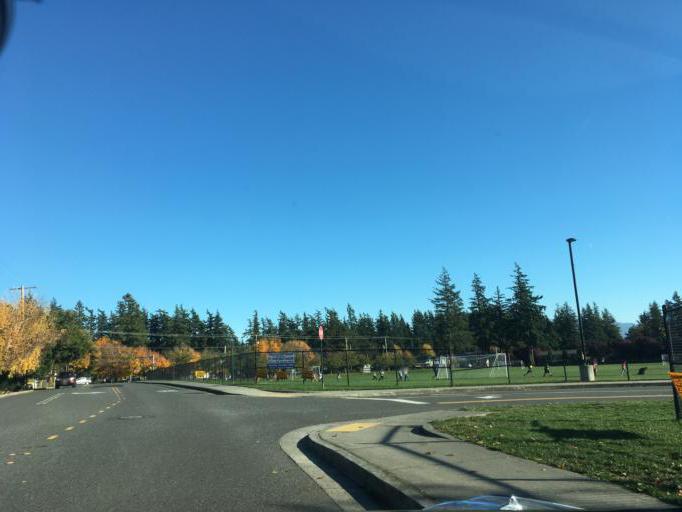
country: US
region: Washington
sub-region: Whatcom County
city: Bellingham
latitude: 48.7799
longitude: -122.5025
